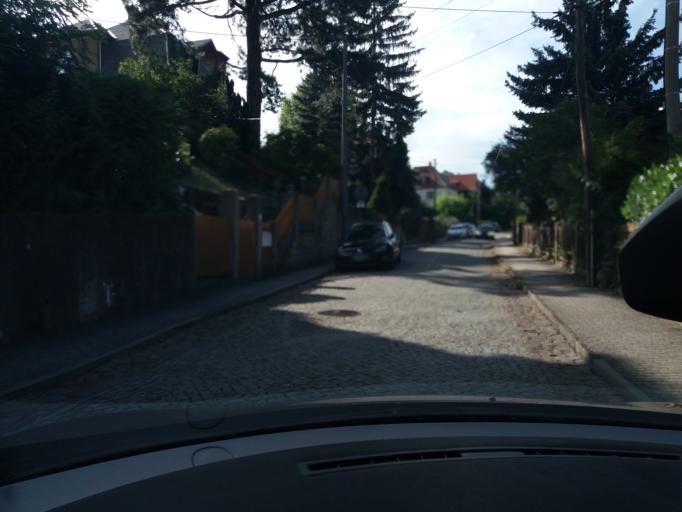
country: DE
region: Saxony
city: Radebeul
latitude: 51.0785
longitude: 13.6501
